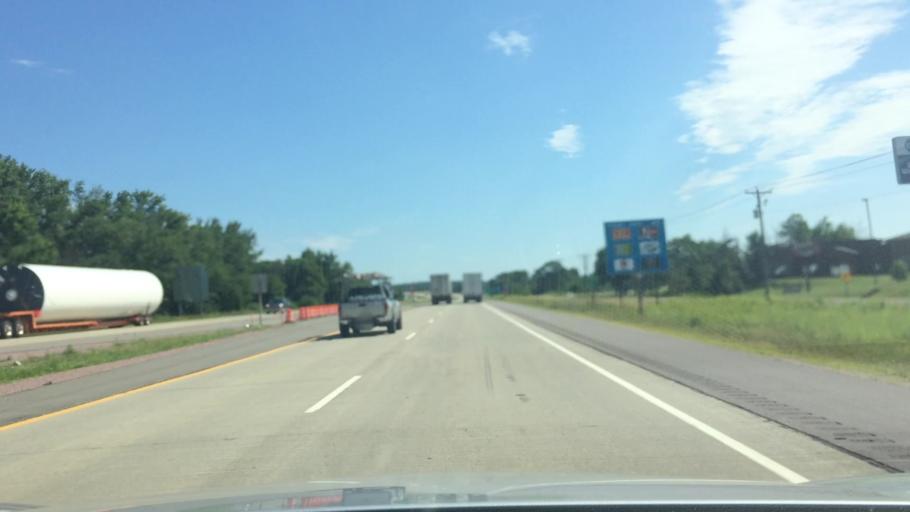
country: US
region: Wisconsin
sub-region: Columbia County
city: Portage
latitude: 43.5701
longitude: -89.4790
